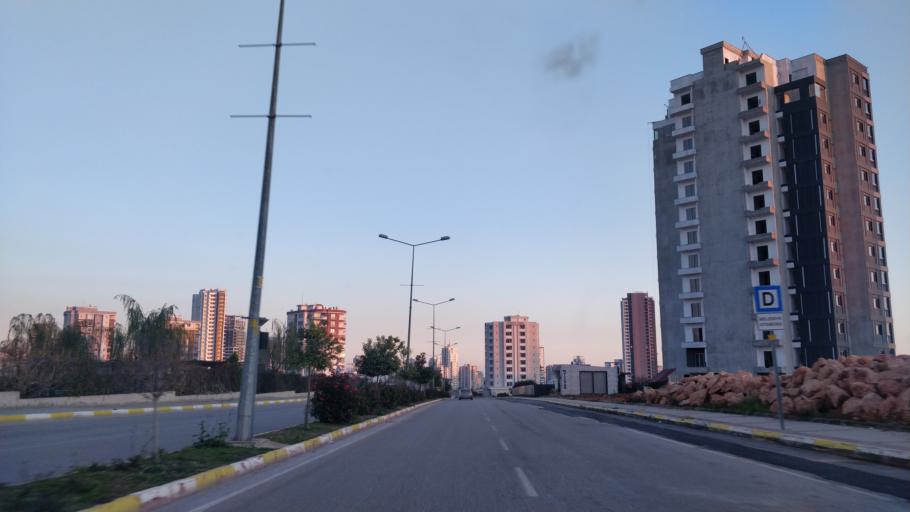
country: TR
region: Mersin
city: Mercin
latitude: 36.8003
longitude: 34.5732
